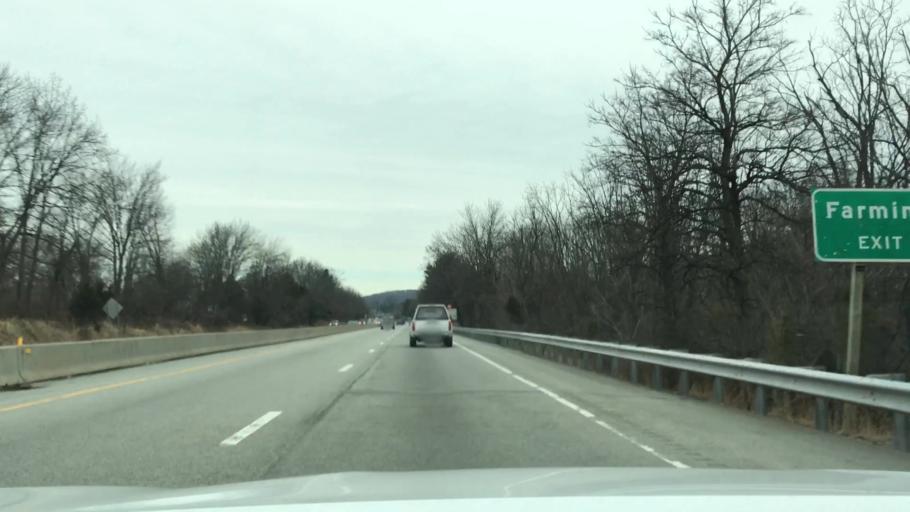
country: US
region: Pennsylvania
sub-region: Montgomery County
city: Halfway House
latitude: 40.2796
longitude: -75.6451
